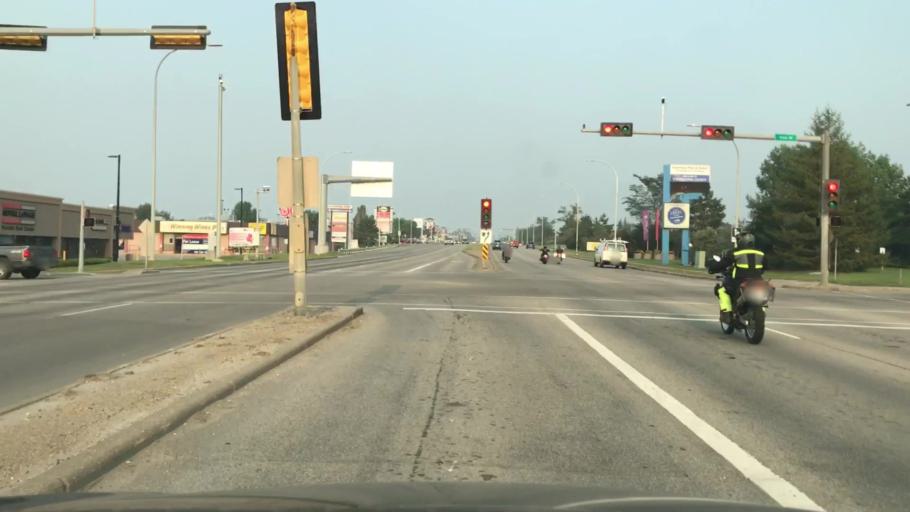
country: CA
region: Alberta
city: Sherwood Park
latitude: 53.5121
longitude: -113.3307
